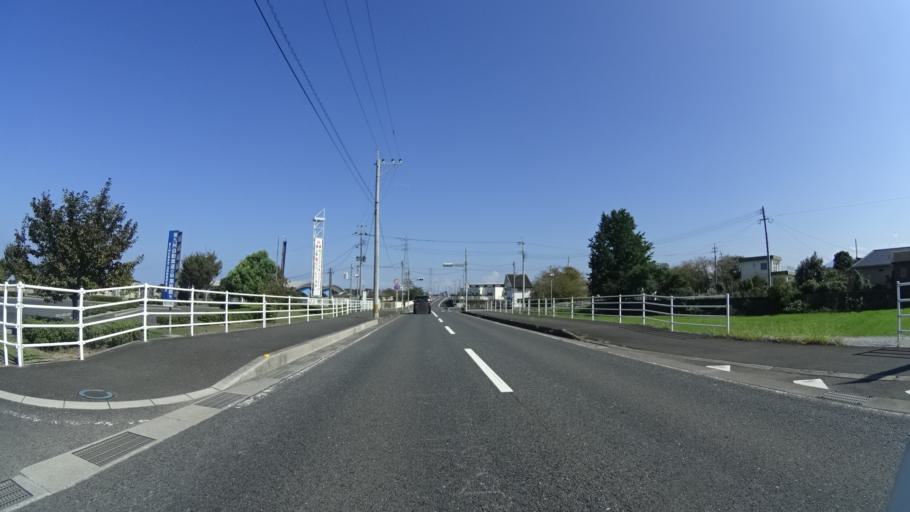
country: JP
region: Fukuoka
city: Tsuiki
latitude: 33.6643
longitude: 131.0297
